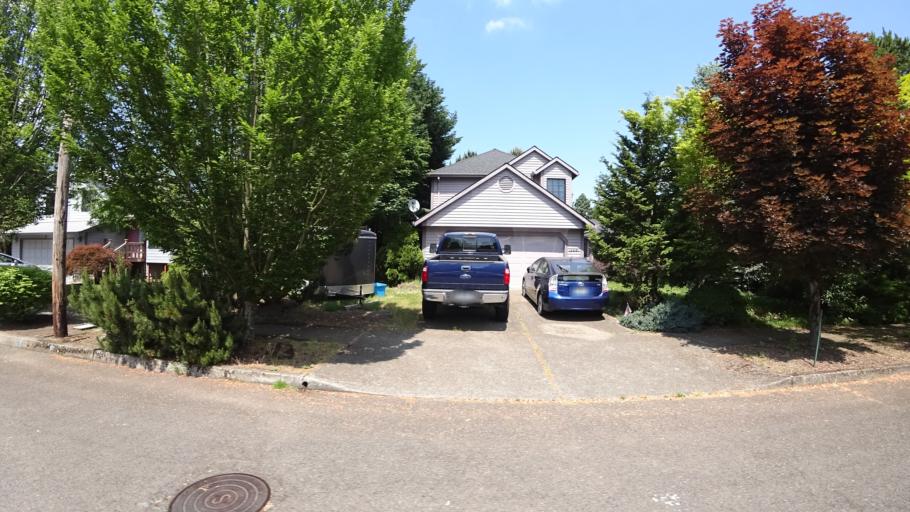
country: US
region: Oregon
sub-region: Multnomah County
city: Fairview
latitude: 45.5367
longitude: -122.4989
